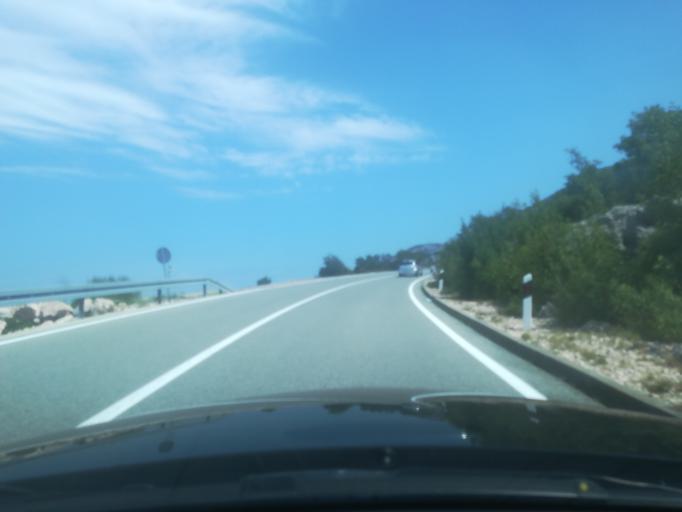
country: HR
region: Primorsko-Goranska
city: Banjol
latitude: 44.8180
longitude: 14.9006
